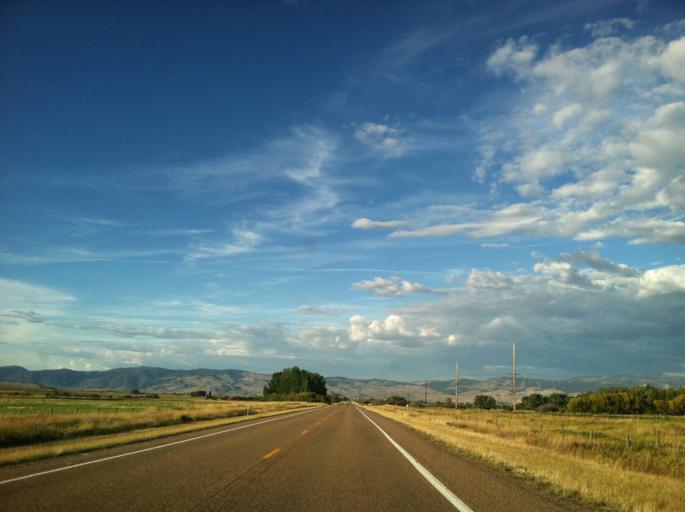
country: US
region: Montana
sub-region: Granite County
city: Philipsburg
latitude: 46.5602
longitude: -113.2135
